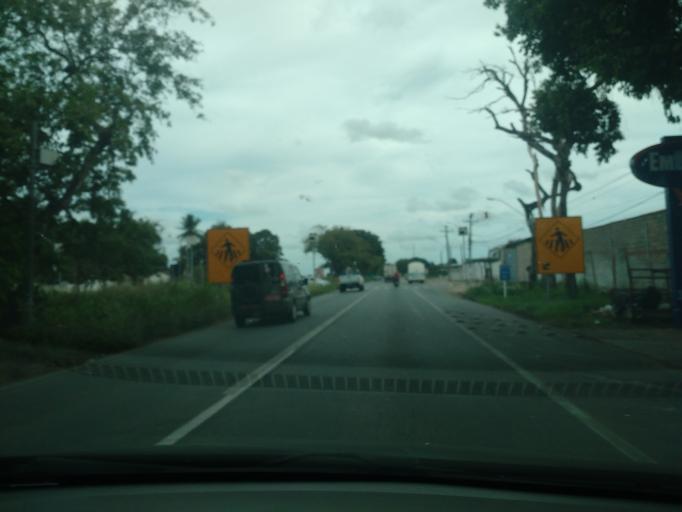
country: BR
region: Alagoas
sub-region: Rio Largo
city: Rio Largo
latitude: -9.4970
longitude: -35.8127
